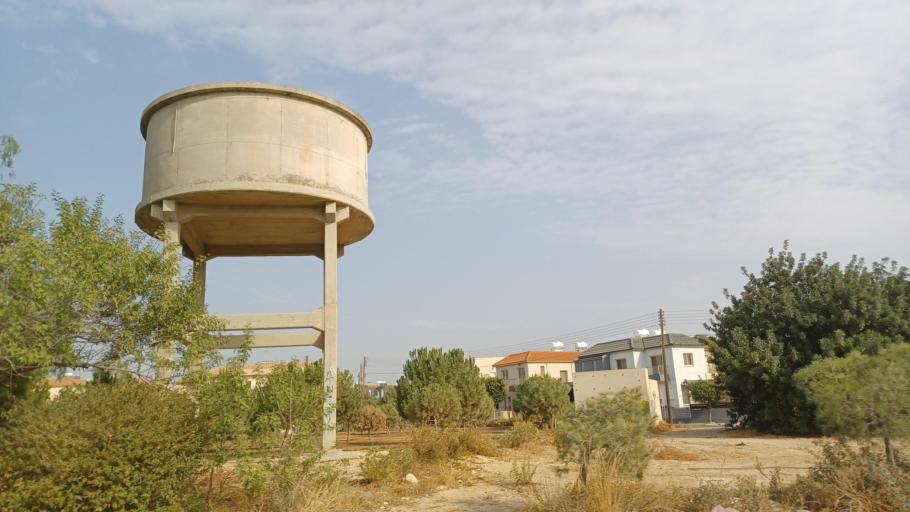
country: CY
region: Limassol
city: Ypsonas
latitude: 34.6943
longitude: 32.9433
